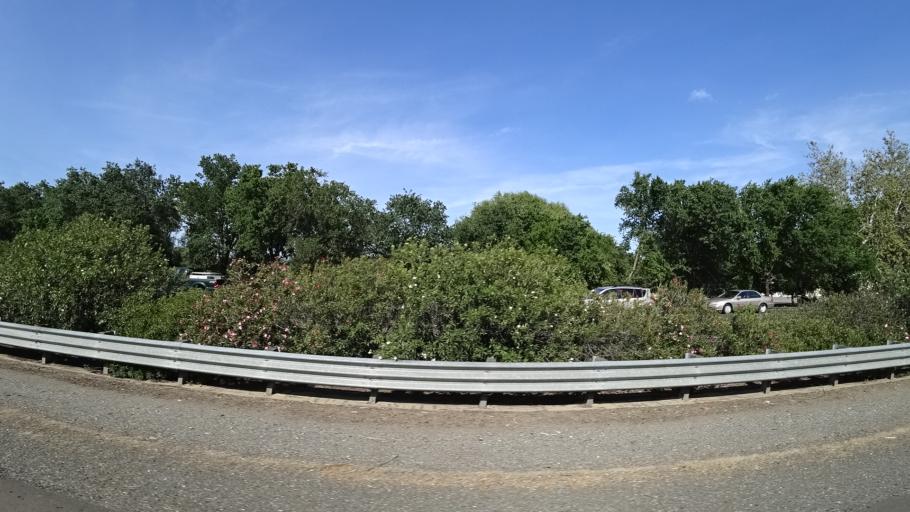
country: US
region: California
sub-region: Butte County
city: Chico
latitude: 39.7315
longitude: -121.8135
